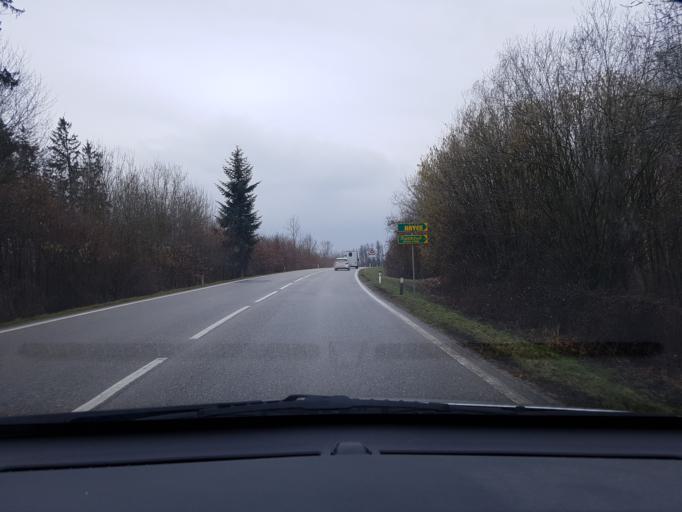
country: AT
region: Upper Austria
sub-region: Steyr Stadt
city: Steyr
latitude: 48.0618
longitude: 14.3885
